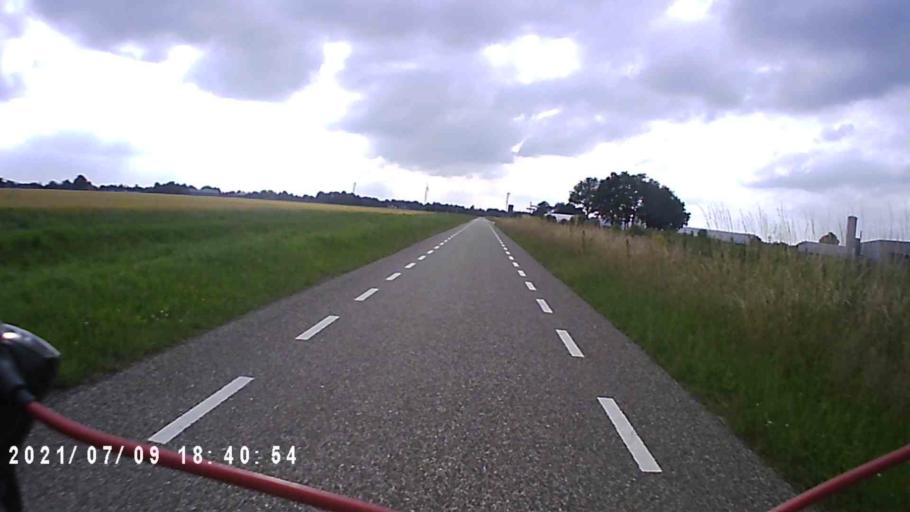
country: NL
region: Groningen
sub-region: Gemeente Veendam
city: Veendam
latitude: 53.0816
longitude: 6.9337
